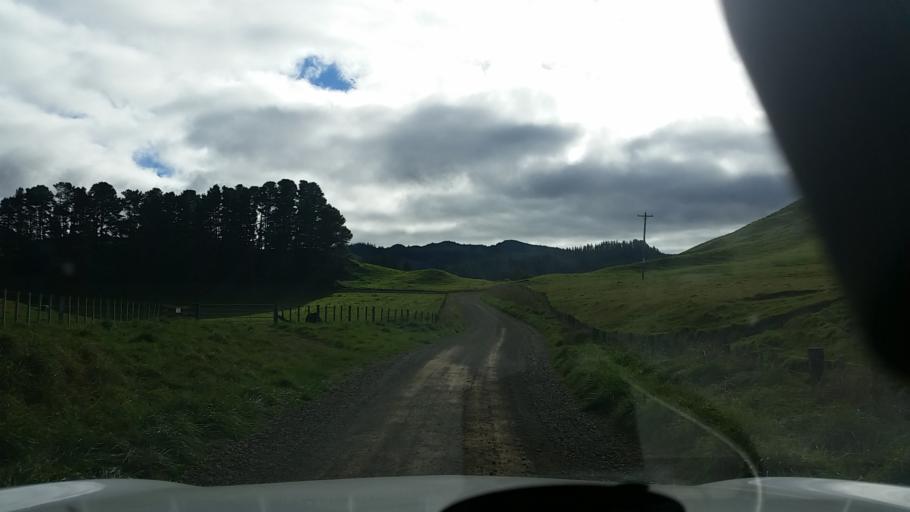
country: NZ
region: Hawke's Bay
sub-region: Napier City
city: Napier
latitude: -39.0982
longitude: 176.8726
